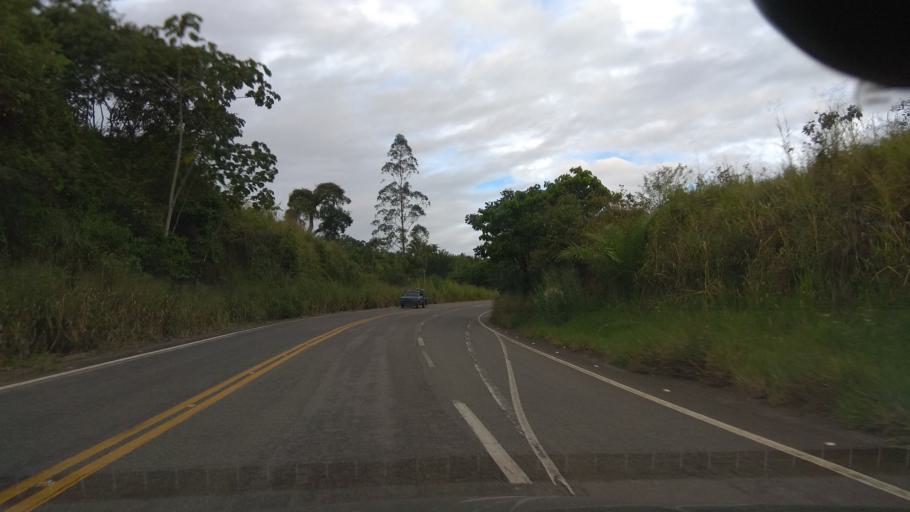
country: BR
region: Bahia
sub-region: Ubaitaba
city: Ubaitaba
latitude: -14.2490
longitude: -39.3763
